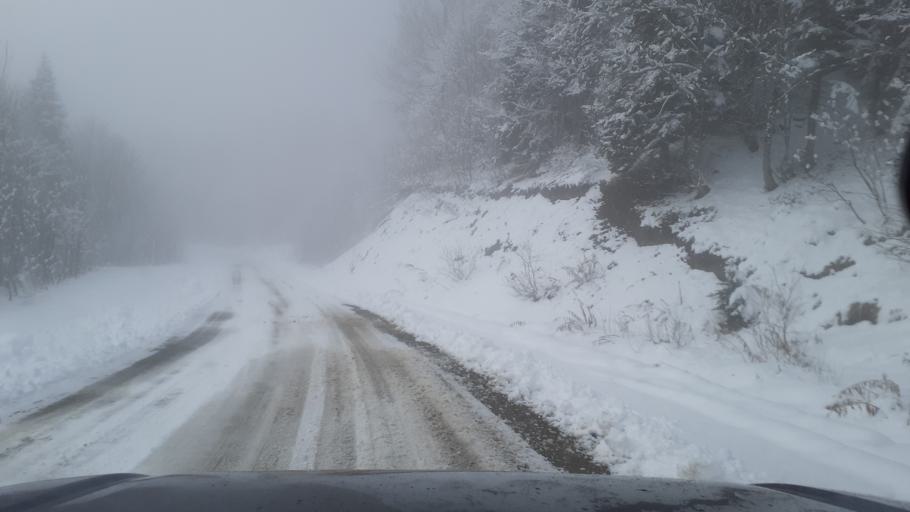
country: RU
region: Adygeya
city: Kamennomostskiy
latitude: 44.0109
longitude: 40.0304
